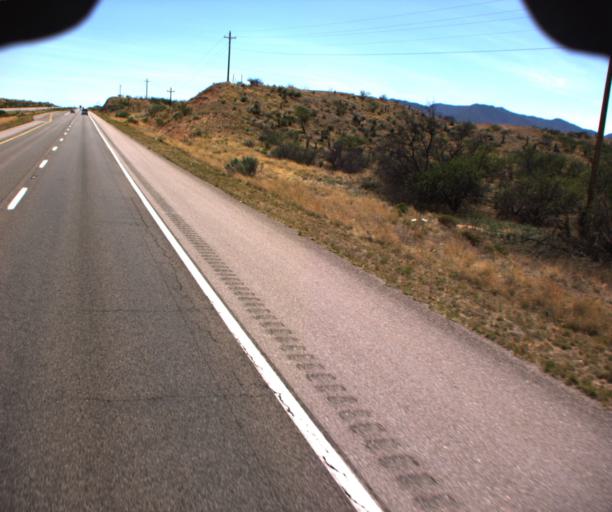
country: US
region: Arizona
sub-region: Cochise County
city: Whetstone
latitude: 31.9375
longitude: -110.3413
